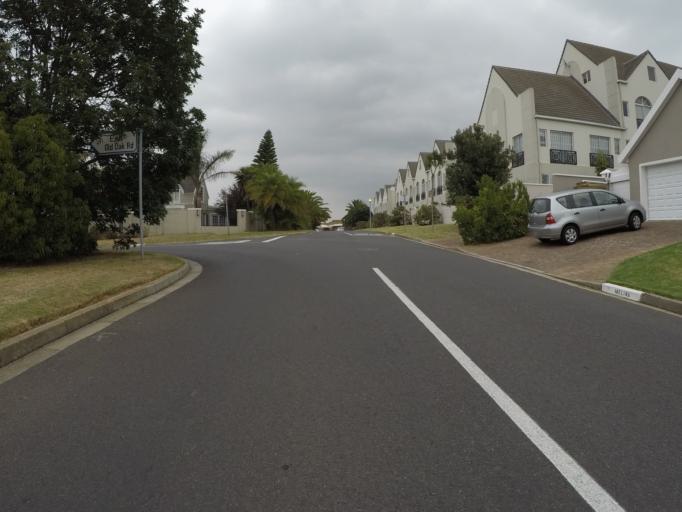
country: ZA
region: Western Cape
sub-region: City of Cape Town
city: Kraaifontein
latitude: -33.8691
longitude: 18.6435
